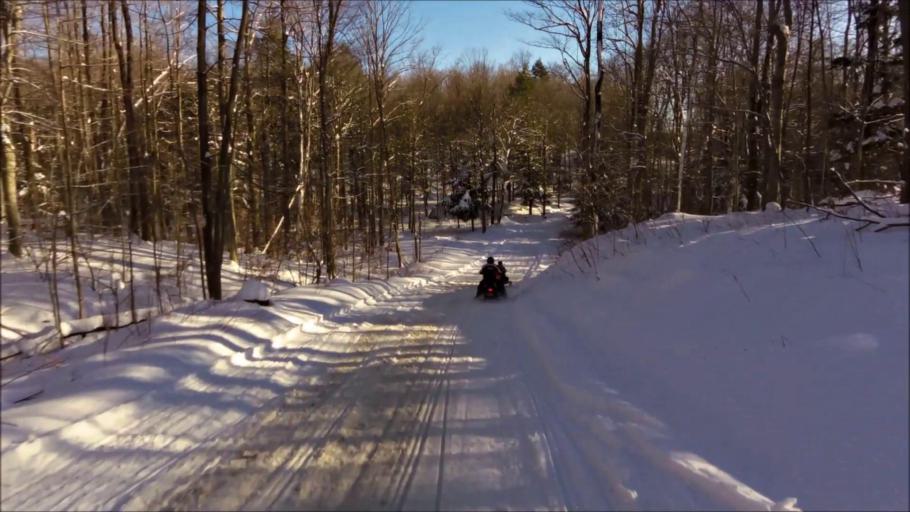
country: US
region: New York
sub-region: Chautauqua County
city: Mayville
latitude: 42.2801
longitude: -79.4140
